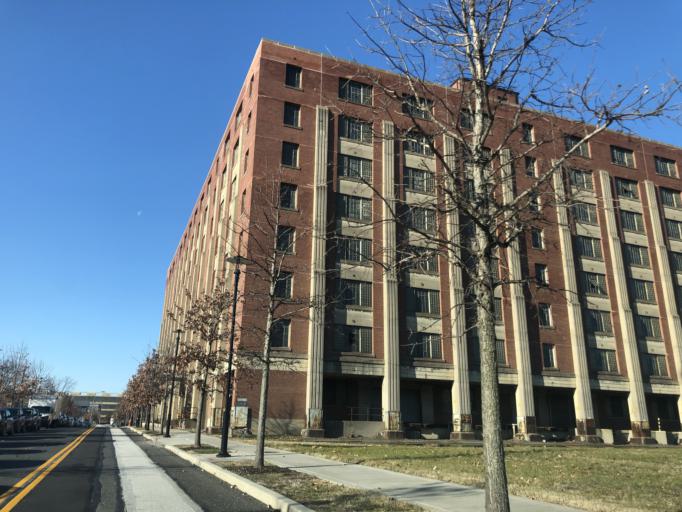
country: US
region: New Jersey
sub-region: Gloucester County
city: National Park
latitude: 39.8892
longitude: -75.1708
